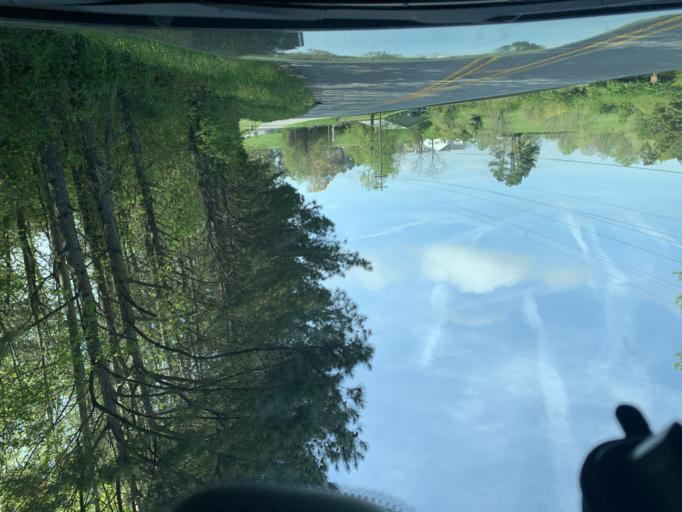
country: US
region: Georgia
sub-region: Forsyth County
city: Cumming
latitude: 34.2398
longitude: -84.0882
